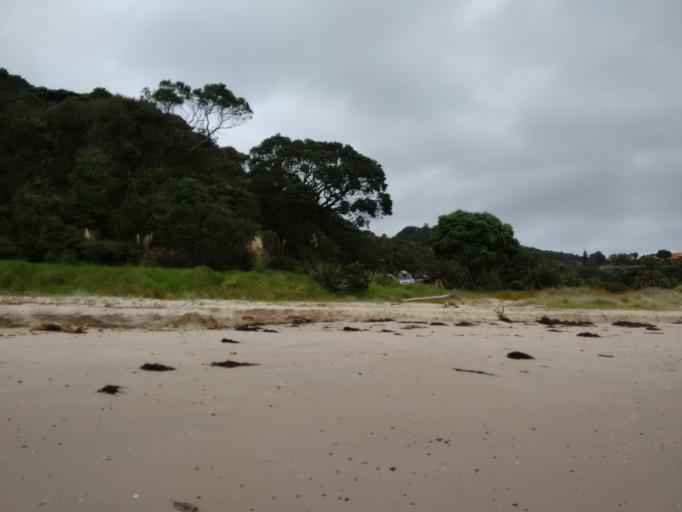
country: NZ
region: Waikato
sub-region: Thames-Coromandel District
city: Whitianga
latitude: -36.7199
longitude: 175.7287
